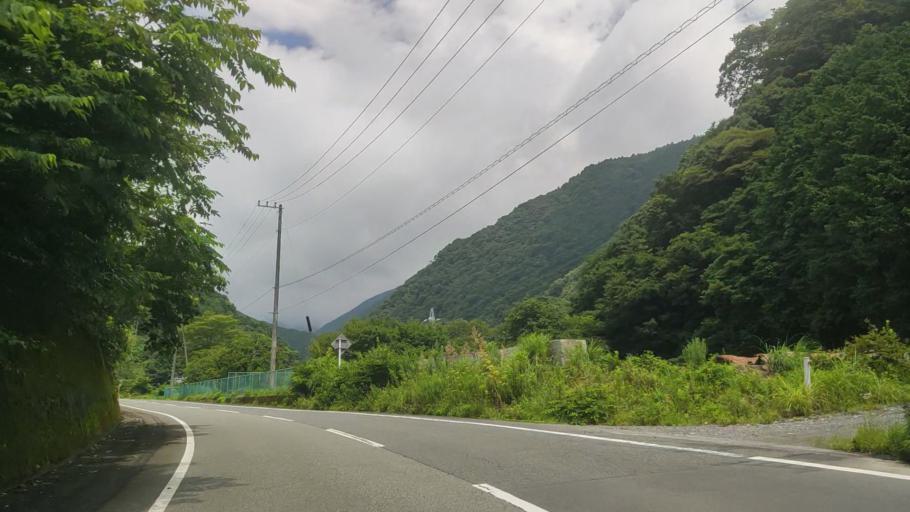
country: JP
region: Shizuoka
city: Fujinomiya
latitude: 35.2365
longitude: 138.5111
